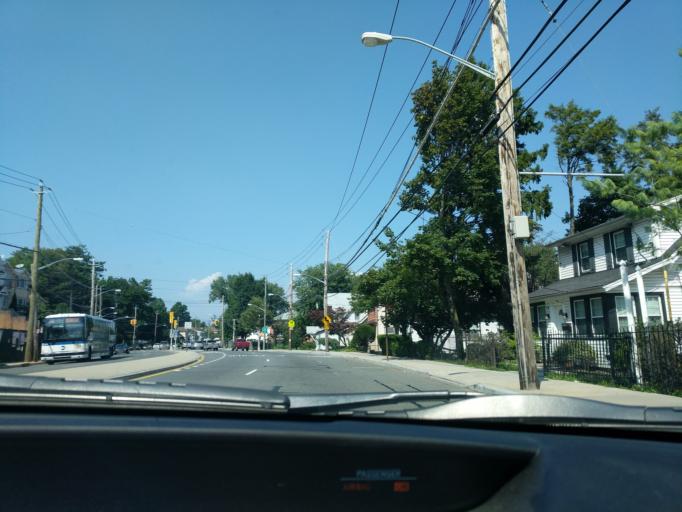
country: US
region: New York
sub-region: Richmond County
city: Staten Island
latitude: 40.5431
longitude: -74.1451
